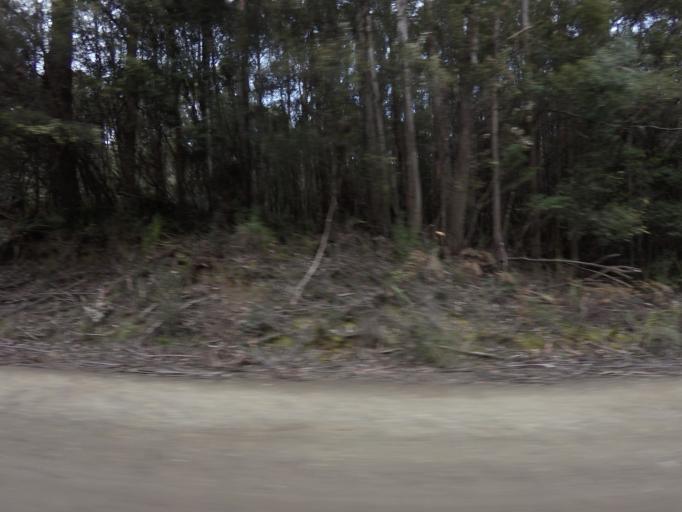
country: AU
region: Tasmania
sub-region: Huon Valley
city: Geeveston
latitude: -43.5234
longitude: 146.8822
